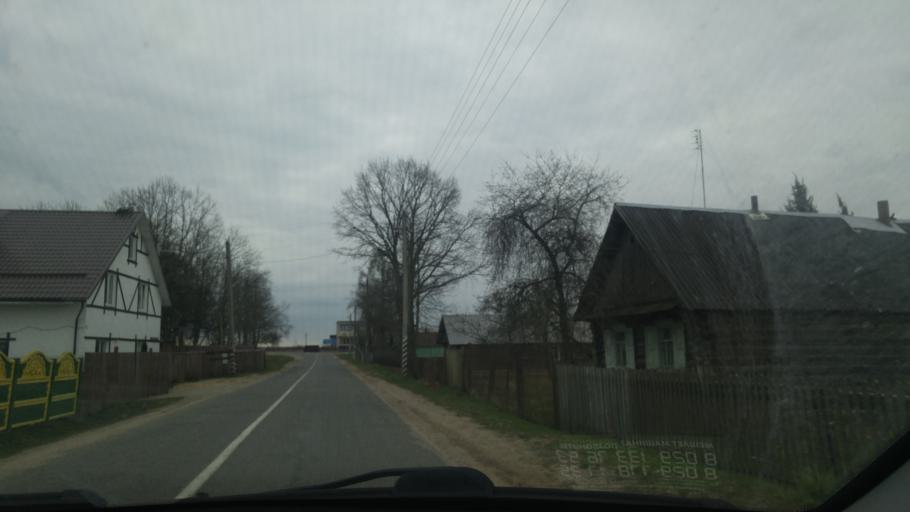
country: BY
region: Minsk
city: Blon'
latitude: 53.6751
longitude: 28.1843
